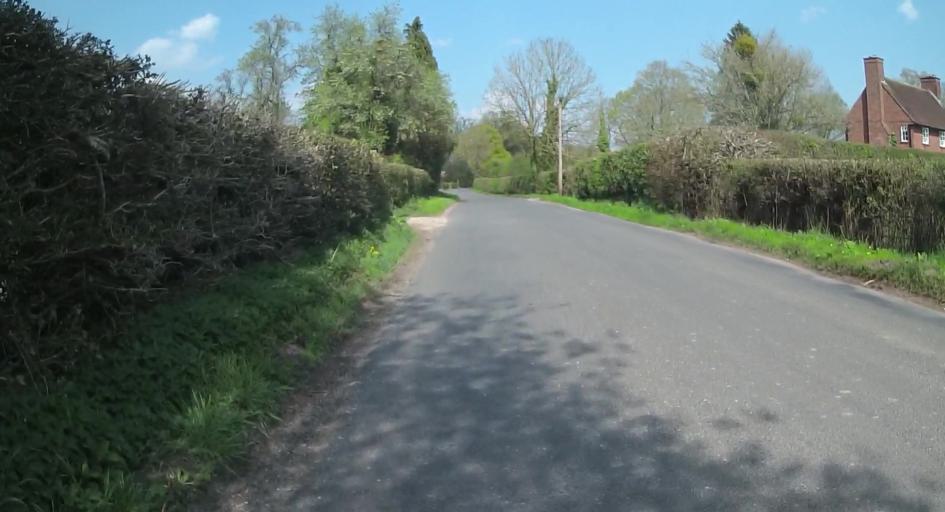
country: GB
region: England
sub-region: Hampshire
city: Basingstoke
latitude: 51.3086
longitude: -1.0861
